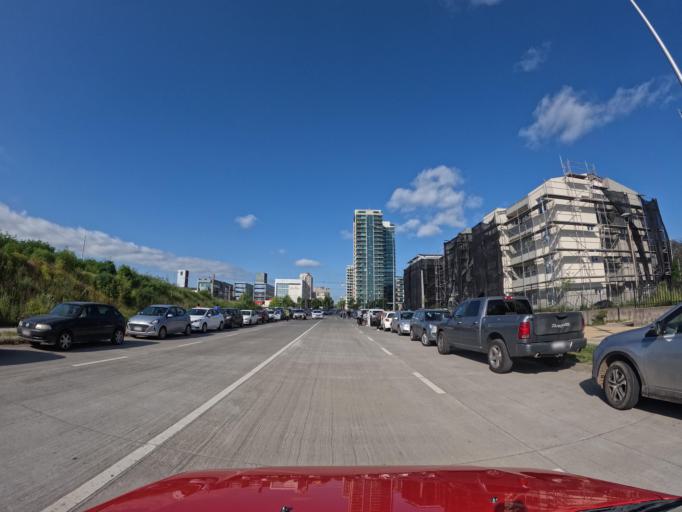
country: CL
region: Biobio
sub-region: Provincia de Concepcion
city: Concepcion
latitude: -36.8323
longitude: -73.0612
